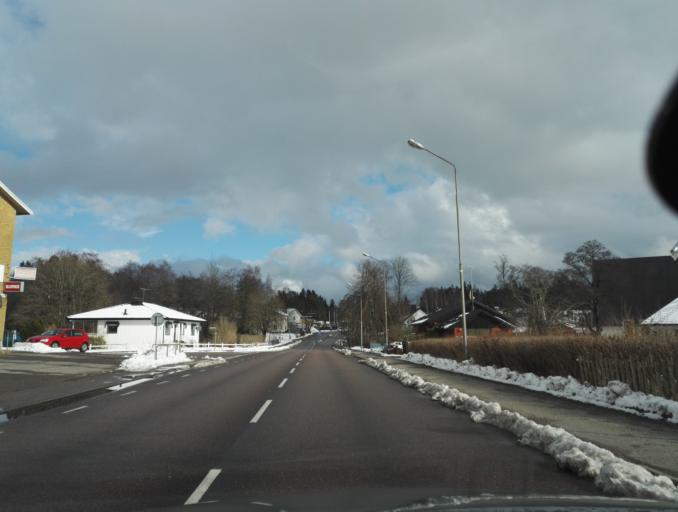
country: SE
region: Vaestra Goetaland
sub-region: Boras Kommun
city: Sandared
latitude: 57.7100
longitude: 12.7949
